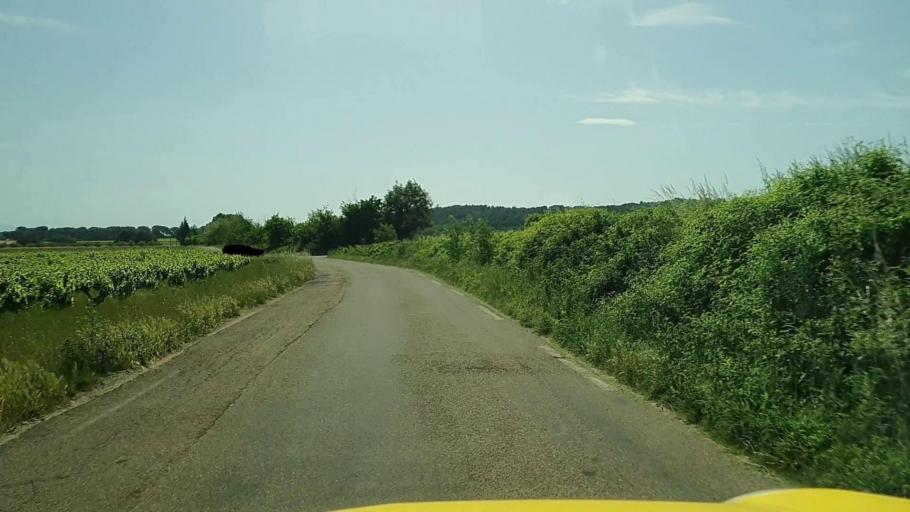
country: FR
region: Languedoc-Roussillon
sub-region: Departement du Gard
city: Tresques
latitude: 44.0937
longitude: 4.5647
